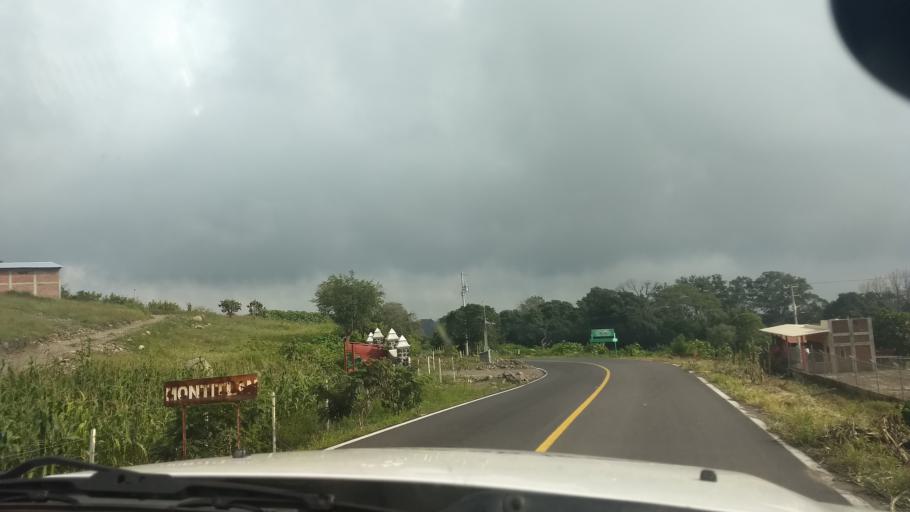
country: MX
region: Colima
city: Queseria
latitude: 19.4054
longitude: -103.6193
